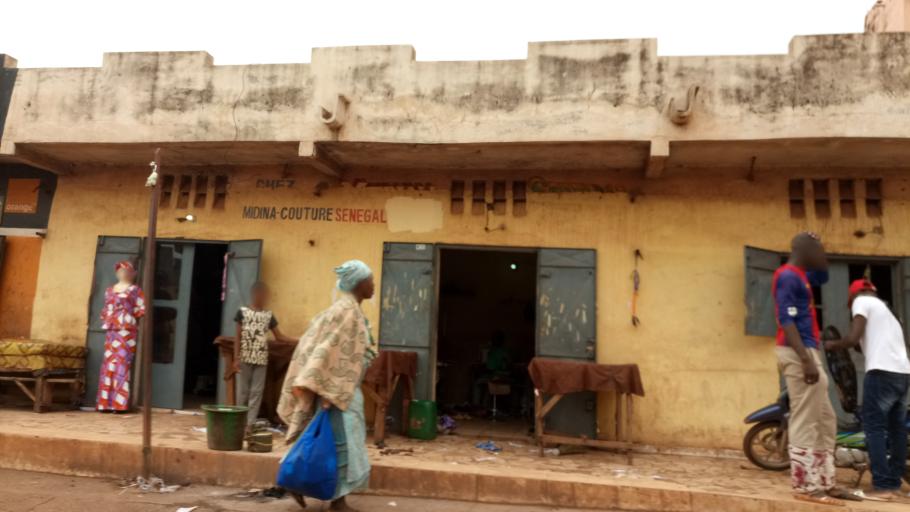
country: ML
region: Bamako
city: Bamako
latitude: 12.5887
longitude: -7.9926
